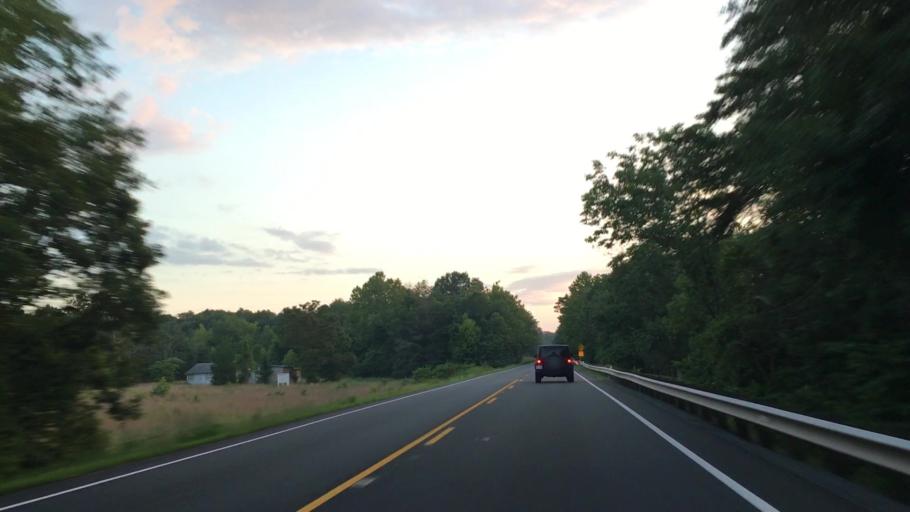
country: US
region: Virginia
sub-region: Culpeper County
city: Culpeper
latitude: 38.2928
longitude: -77.8549
